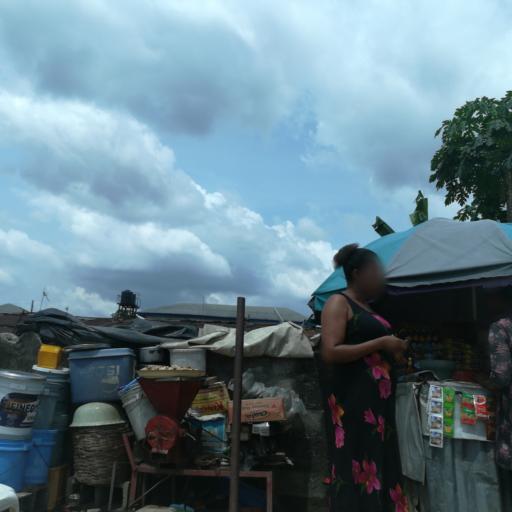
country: NG
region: Rivers
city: Okrika
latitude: 4.7758
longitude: 7.0601
